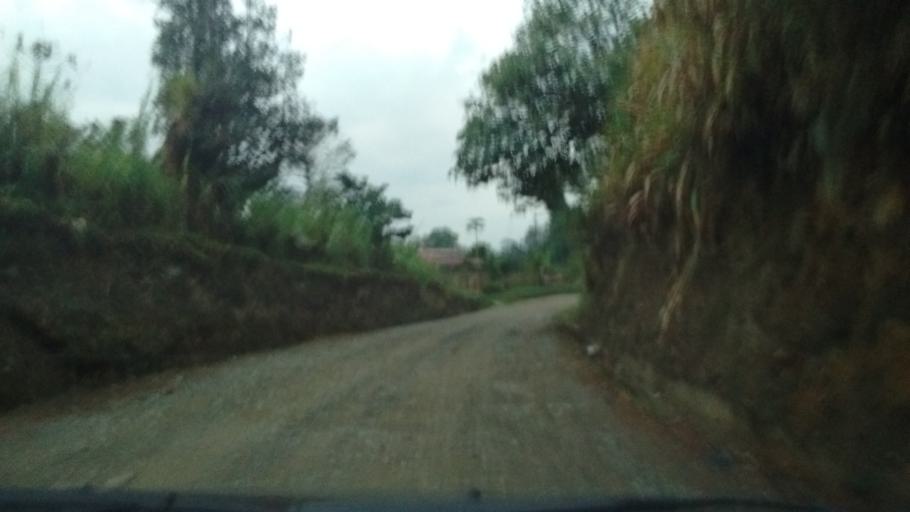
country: CO
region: Cauca
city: Lopez
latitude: 2.3792
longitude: -76.7125
